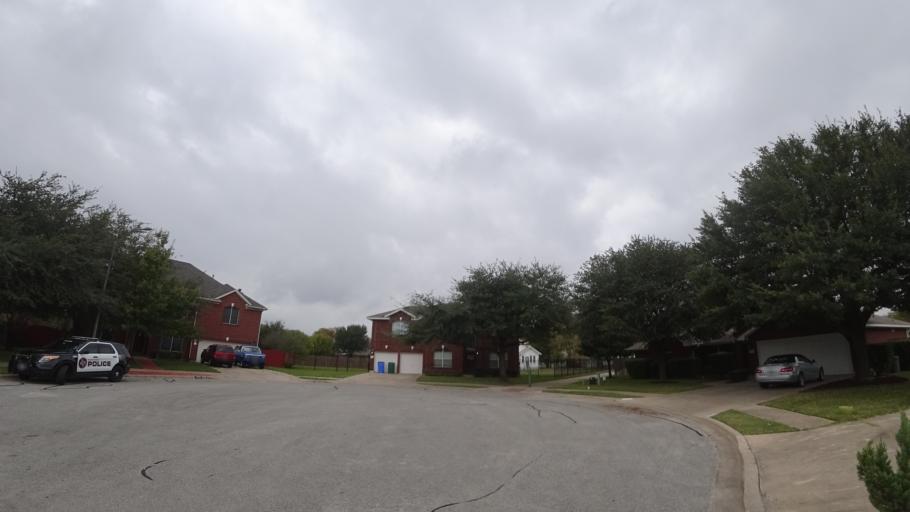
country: US
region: Texas
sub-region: Travis County
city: Pflugerville
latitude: 30.4414
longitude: -97.6059
